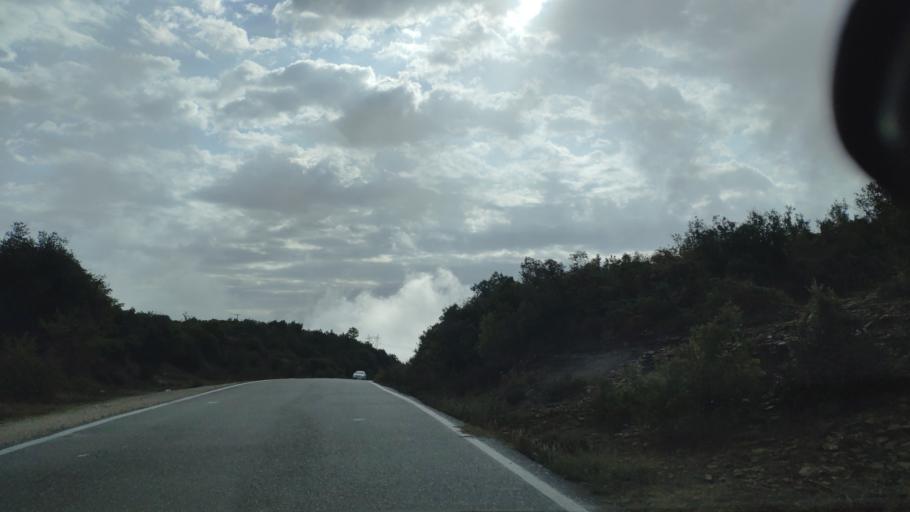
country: GR
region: West Greece
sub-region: Nomos Aitolias kai Akarnanias
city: Sardinia
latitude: 38.8768
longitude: 21.2674
